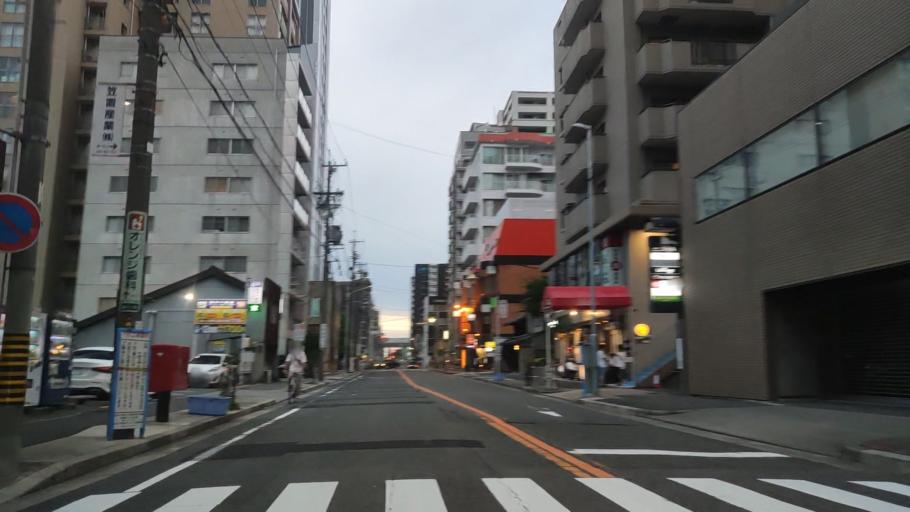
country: JP
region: Aichi
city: Nagoya-shi
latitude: 35.1747
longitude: 136.9101
